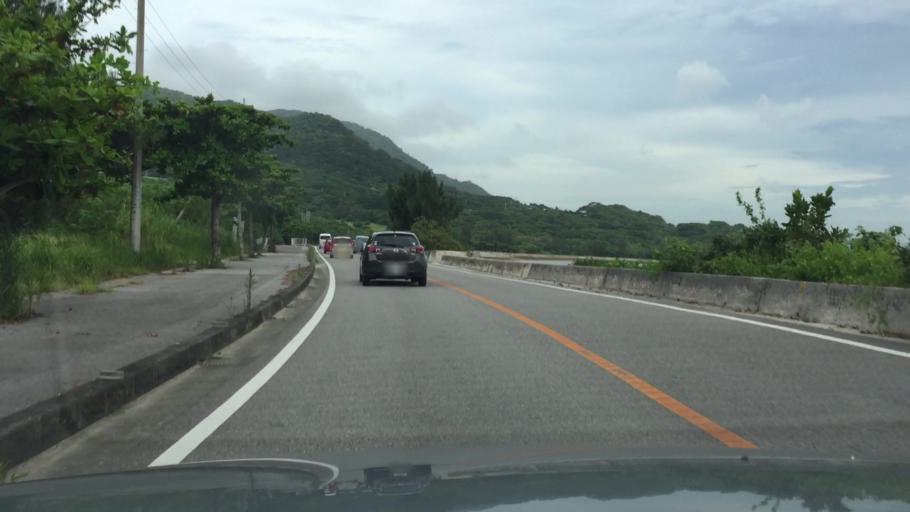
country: JP
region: Okinawa
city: Ishigaki
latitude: 24.4347
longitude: 124.1203
